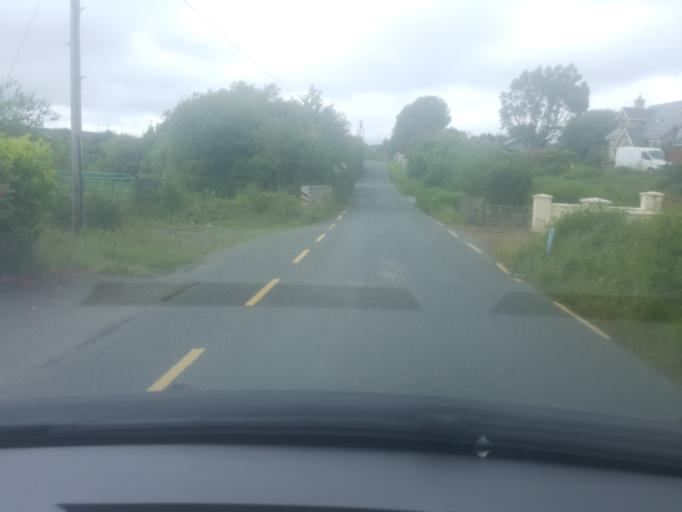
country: IE
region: Munster
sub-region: Ciarrai
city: Cill Airne
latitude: 52.1098
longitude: -9.5057
